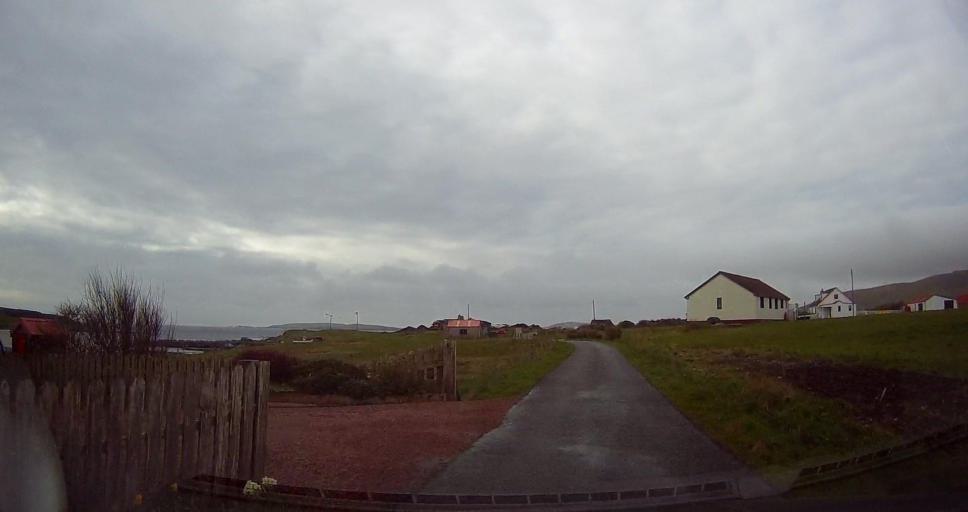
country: GB
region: Scotland
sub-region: Shetland Islands
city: Sandwick
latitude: 60.0400
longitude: -1.2186
